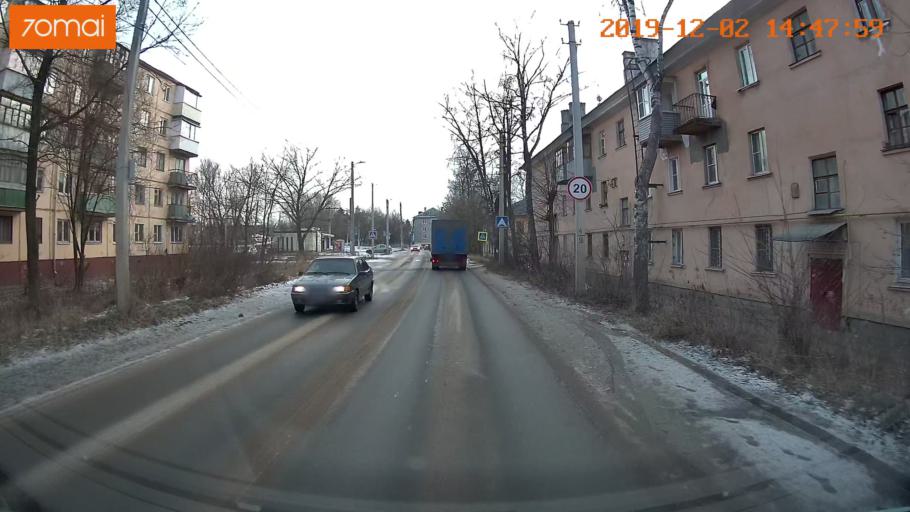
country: RU
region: Ivanovo
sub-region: Gorod Ivanovo
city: Ivanovo
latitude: 56.9860
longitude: 41.0175
